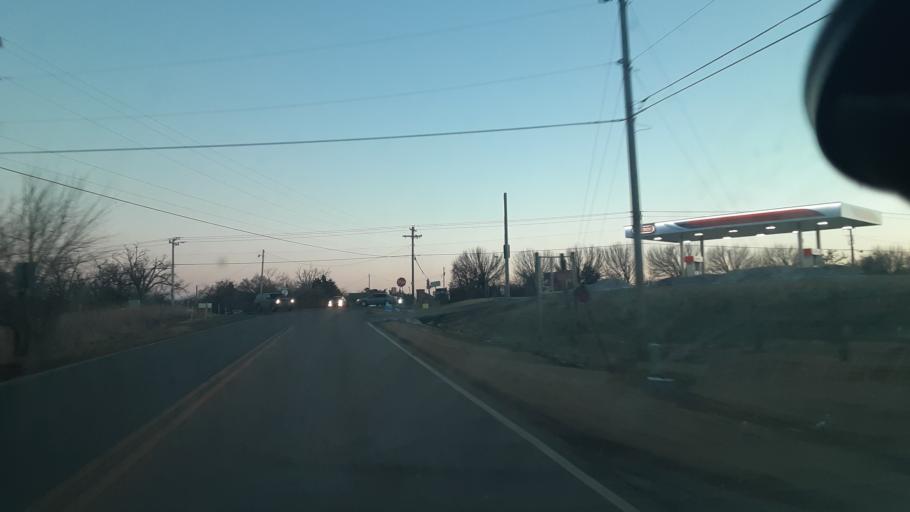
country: US
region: Oklahoma
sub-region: Oklahoma County
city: Edmond
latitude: 35.7260
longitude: -97.4254
